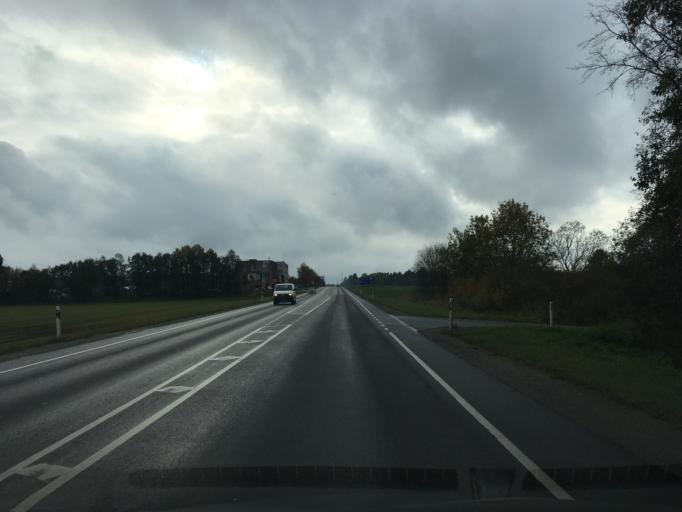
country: EE
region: Harju
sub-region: Keila linn
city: Keila
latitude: 59.3317
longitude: 24.4753
